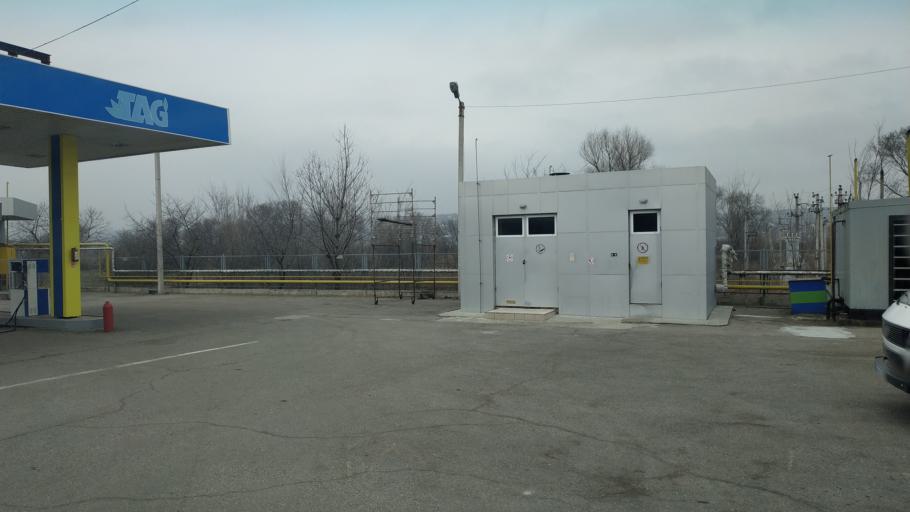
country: MD
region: Chisinau
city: Singera
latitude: 46.9260
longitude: 28.9982
